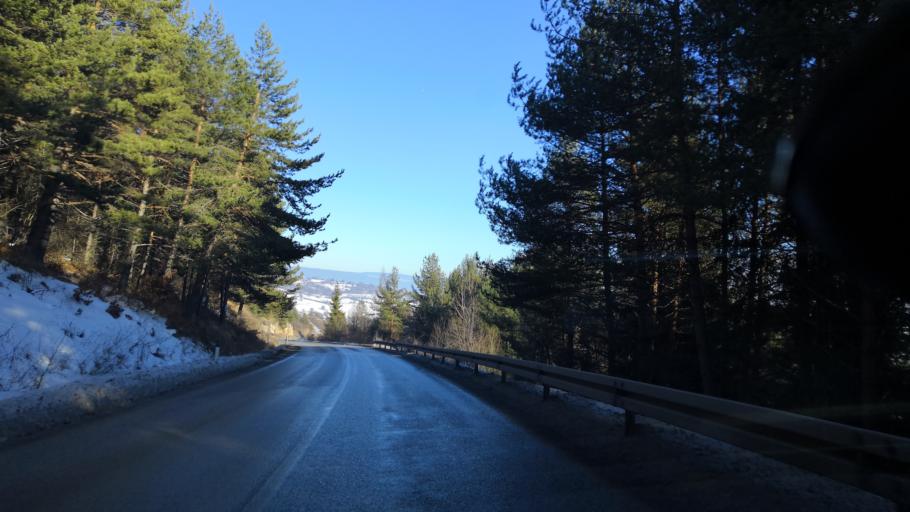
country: BA
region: Republika Srpska
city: Sokolac
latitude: 43.9208
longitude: 18.7440
